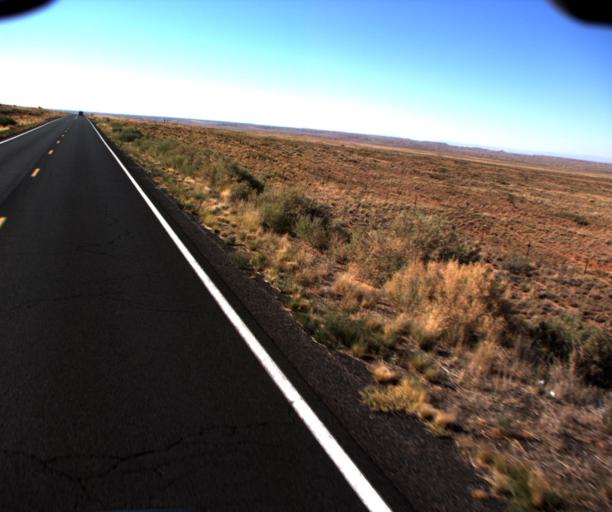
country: US
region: Arizona
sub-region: Navajo County
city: Dilkon
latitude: 35.2994
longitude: -110.4242
